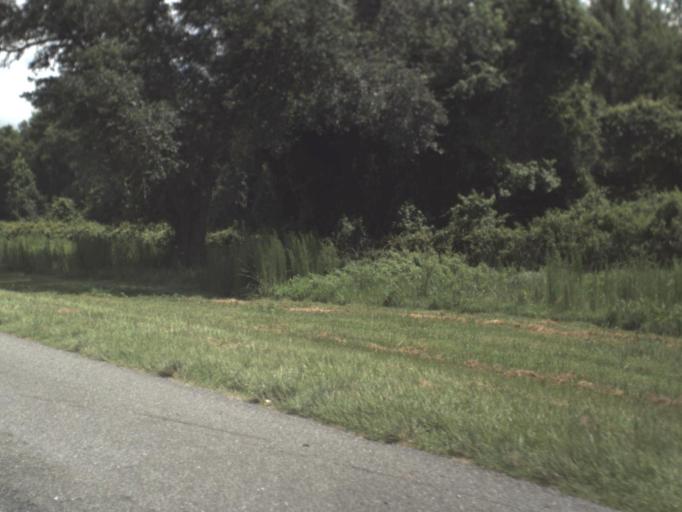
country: US
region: Florida
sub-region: Suwannee County
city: Wellborn
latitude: 30.2560
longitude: -82.7482
